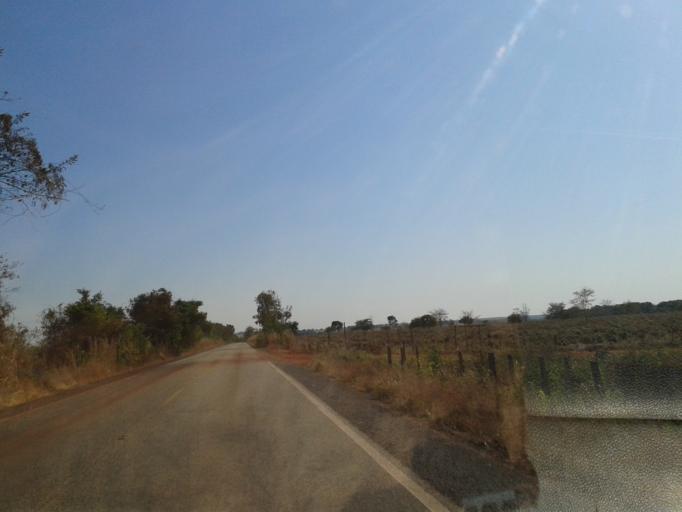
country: BR
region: Goias
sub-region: Mozarlandia
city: Mozarlandia
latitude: -14.6288
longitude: -50.5189
